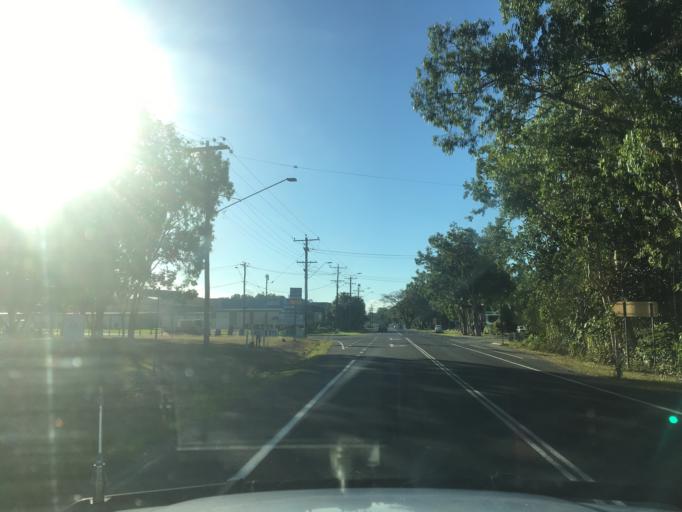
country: AU
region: Queensland
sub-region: Cairns
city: Port Douglas
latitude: -16.5391
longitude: 145.4697
